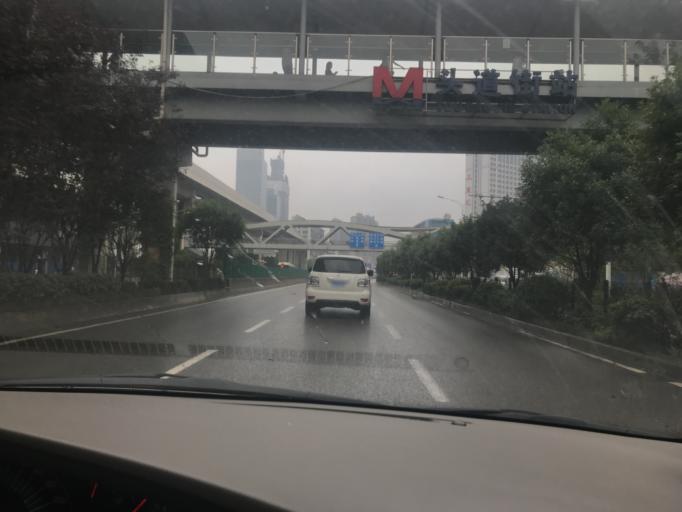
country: CN
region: Hubei
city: Jiang'an
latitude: 30.6204
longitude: 114.3084
